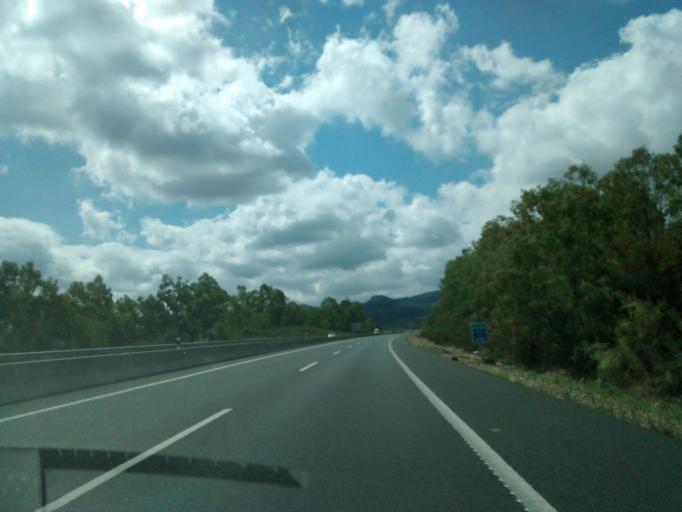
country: ES
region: Extremadura
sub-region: Provincia de Caceres
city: Romangordo
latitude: 39.7231
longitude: -5.7128
